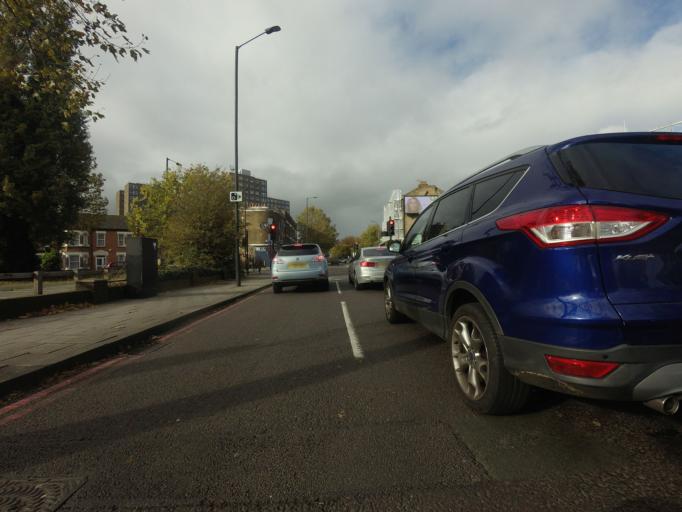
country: GB
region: England
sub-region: Greater London
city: Camberwell
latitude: 51.4806
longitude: -0.0596
